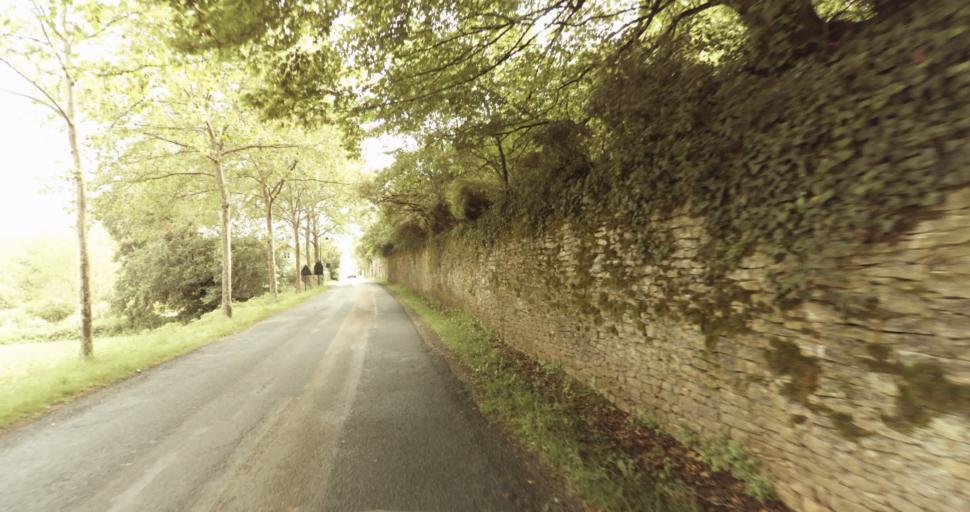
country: FR
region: Aquitaine
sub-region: Departement de la Dordogne
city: Vergt
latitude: 44.9442
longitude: 0.8062
